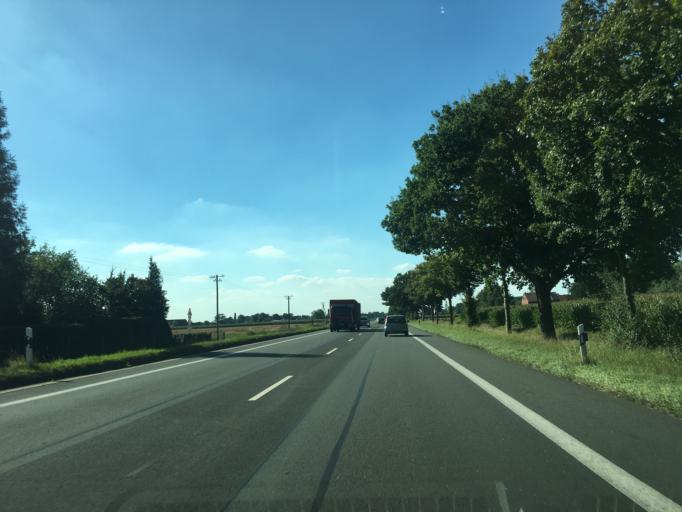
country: DE
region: North Rhine-Westphalia
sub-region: Regierungsbezirk Munster
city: Beelen
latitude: 51.9212
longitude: 8.1444
